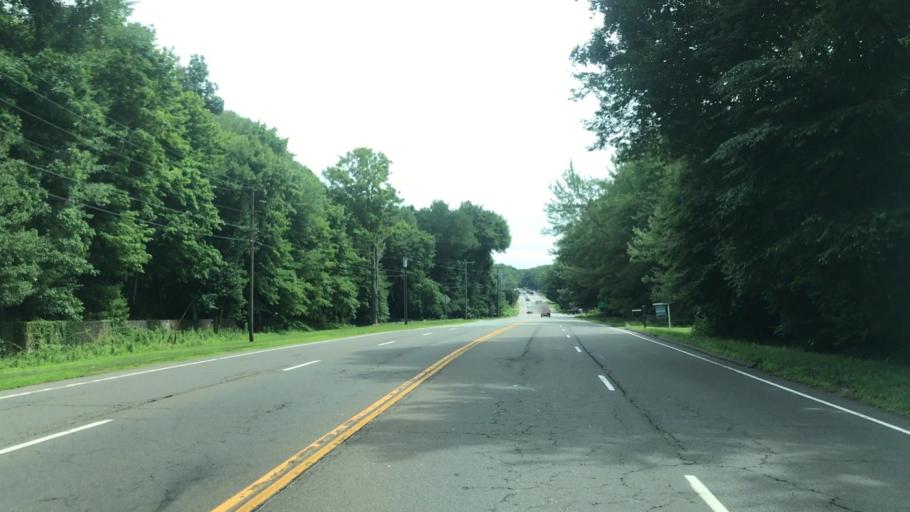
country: US
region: Connecticut
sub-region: Middlesex County
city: Old Saybrook Center
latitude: 41.3190
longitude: -72.3386
